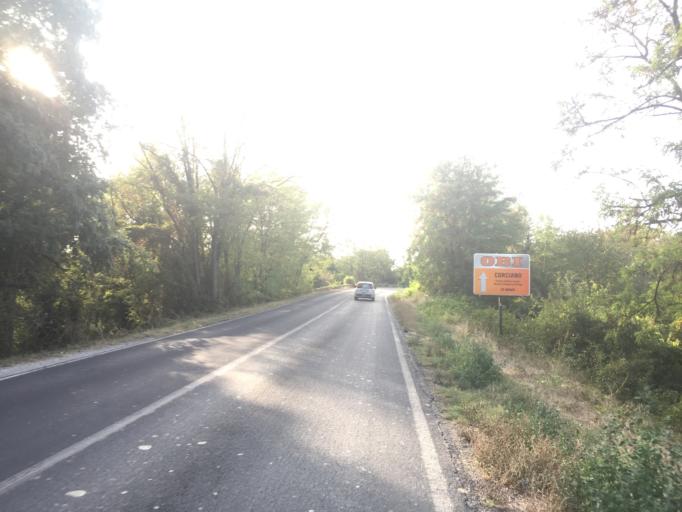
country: IT
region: Umbria
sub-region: Provincia di Perugia
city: Torgiano
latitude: 43.0338
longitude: 12.4242
